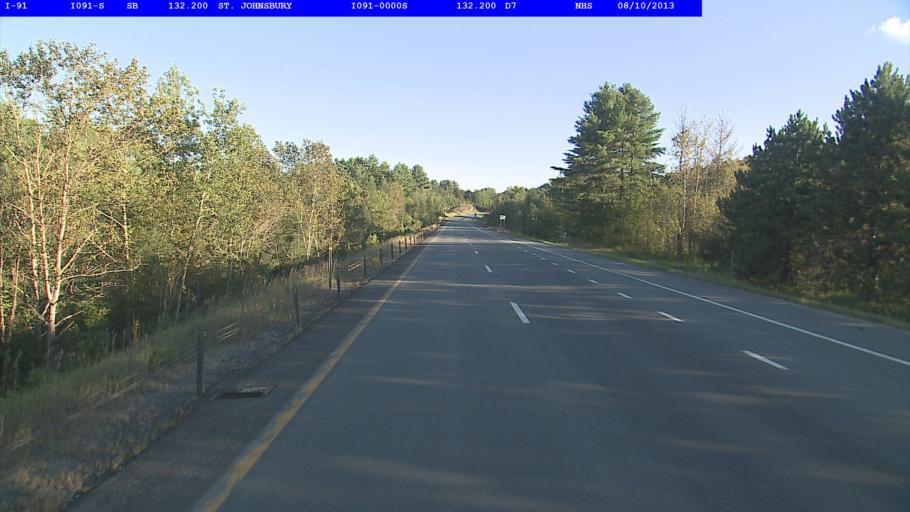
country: US
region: Vermont
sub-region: Caledonia County
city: St Johnsbury
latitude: 44.4484
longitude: -72.0249
